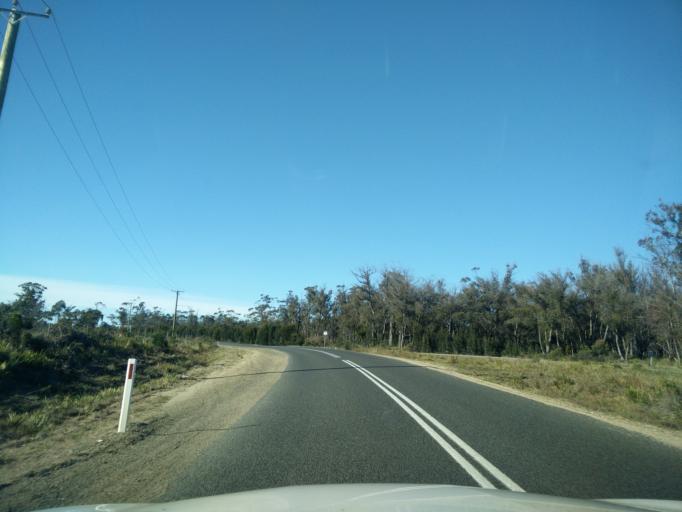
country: AU
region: Tasmania
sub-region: Break O'Day
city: St Helens
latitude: -41.8965
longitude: 148.2555
